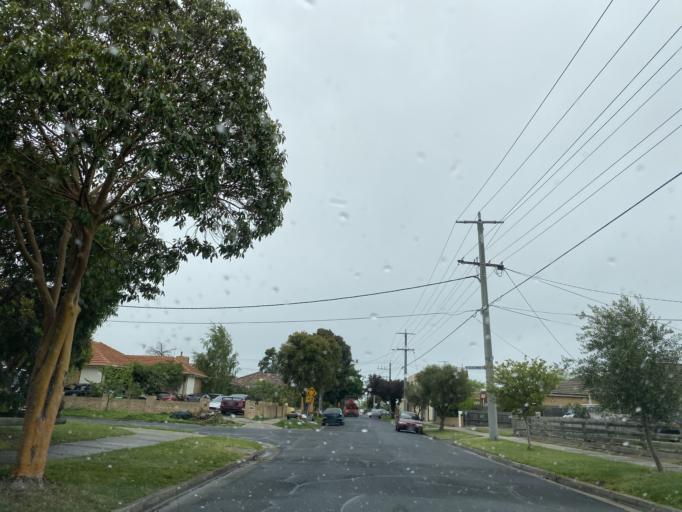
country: AU
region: Victoria
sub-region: Moreland
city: Fawkner
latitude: -37.7099
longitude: 144.9664
